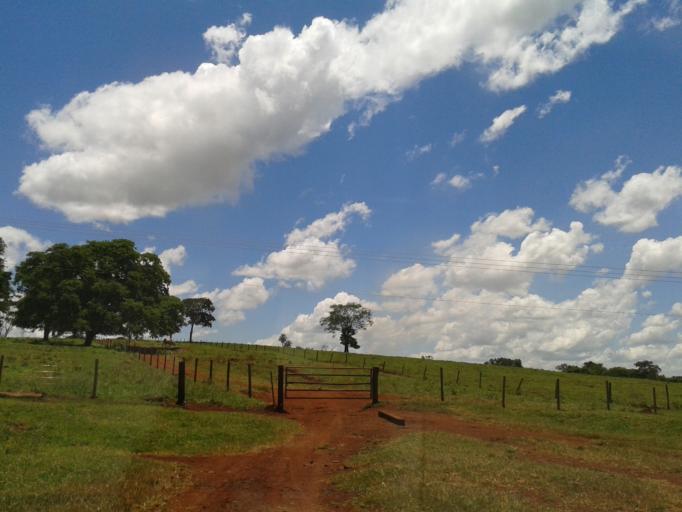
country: BR
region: Minas Gerais
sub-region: Centralina
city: Centralina
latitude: -18.7006
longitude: -49.1774
